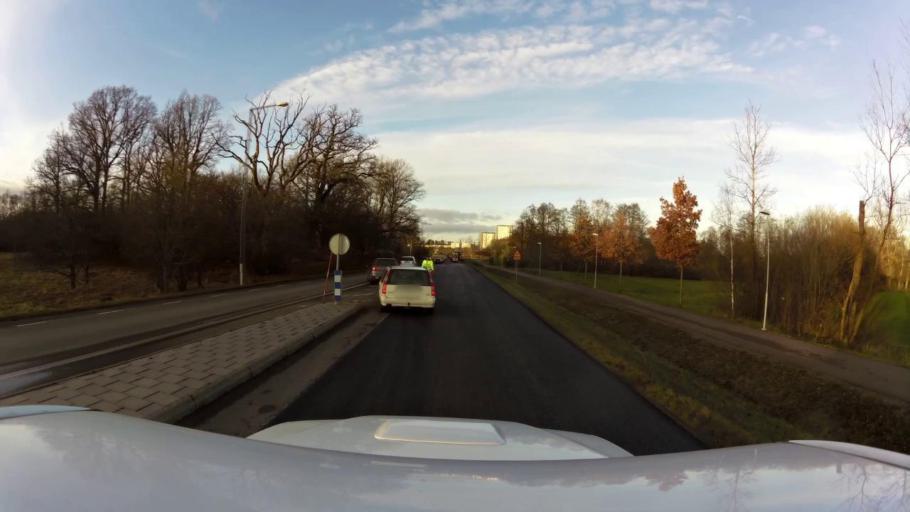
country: SE
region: OEstergoetland
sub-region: Linkopings Kommun
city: Linkoping
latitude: 58.3847
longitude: 15.6302
